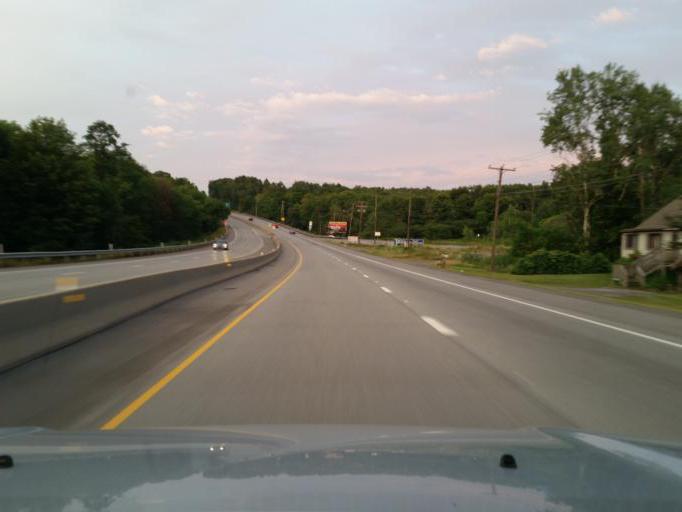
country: US
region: Pennsylvania
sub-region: Cambria County
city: Mundys Corner
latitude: 40.4466
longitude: -78.8022
